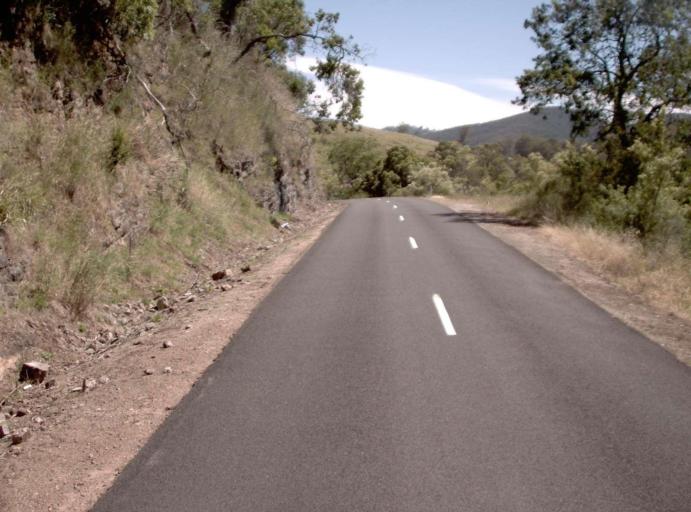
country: AU
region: Victoria
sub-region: East Gippsland
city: Lakes Entrance
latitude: -37.4107
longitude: 148.2095
